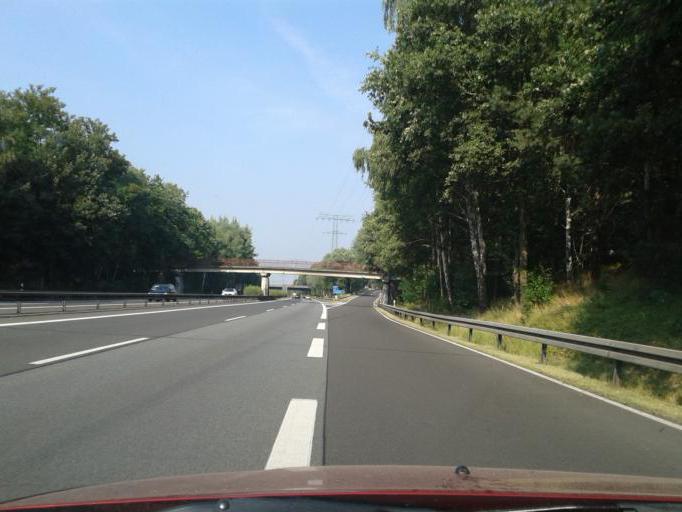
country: DE
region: Brandenburg
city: Birkenwerder
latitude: 52.6997
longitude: 13.2811
